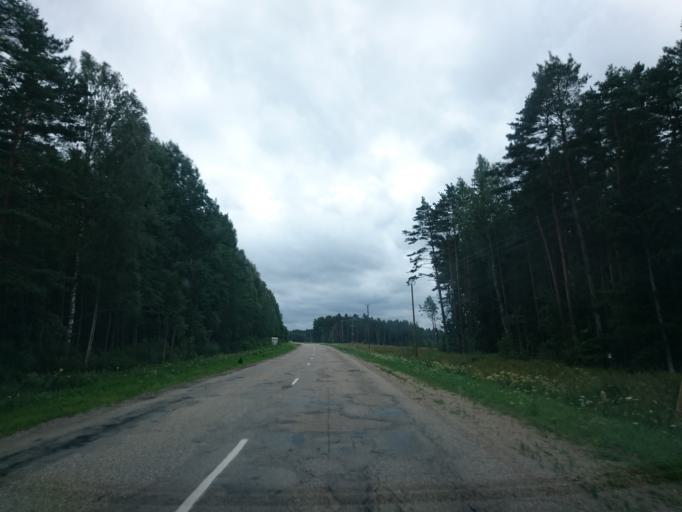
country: LV
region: Pavilostas
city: Pavilosta
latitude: 56.8049
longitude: 21.2270
